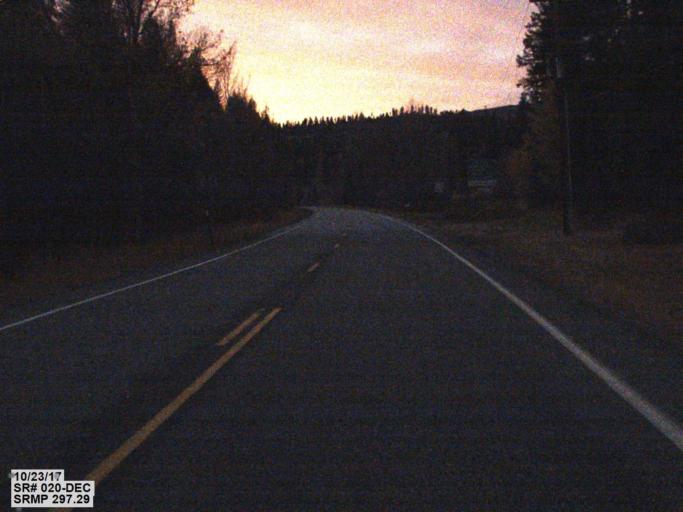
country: US
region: Washington
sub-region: Ferry County
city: Republic
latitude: 48.6612
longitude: -118.8356
